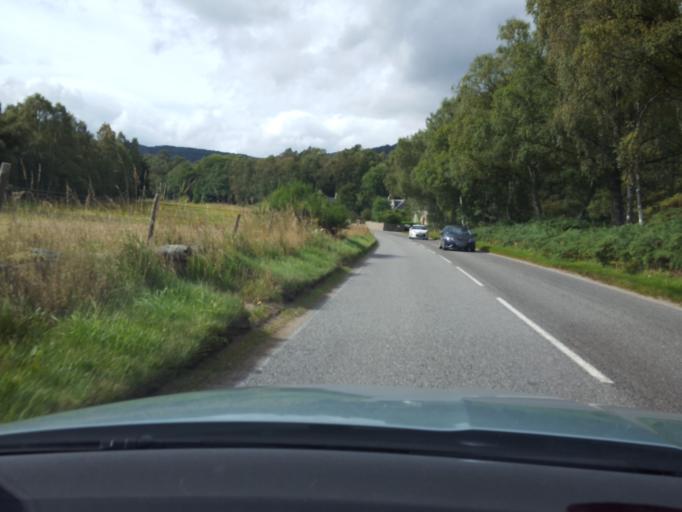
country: GB
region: Scotland
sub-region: Aberdeenshire
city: Ballater
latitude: 57.0710
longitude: -2.9674
